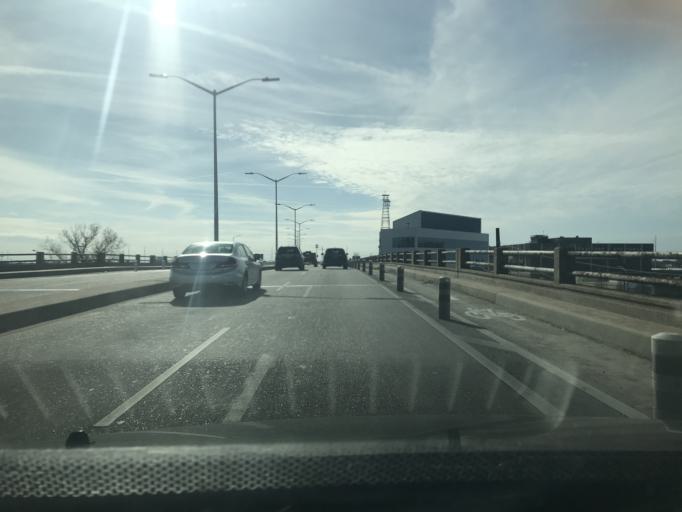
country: US
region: Louisiana
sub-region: Orleans Parish
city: New Orleans
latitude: 29.9585
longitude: -90.0935
